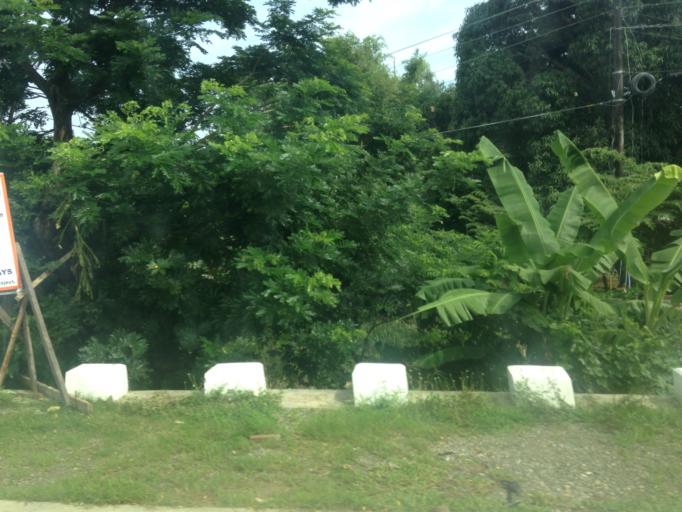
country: PH
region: Mimaropa
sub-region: Province of Mindoro Oriental
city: Bulalacao
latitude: 12.3838
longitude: 121.3512
